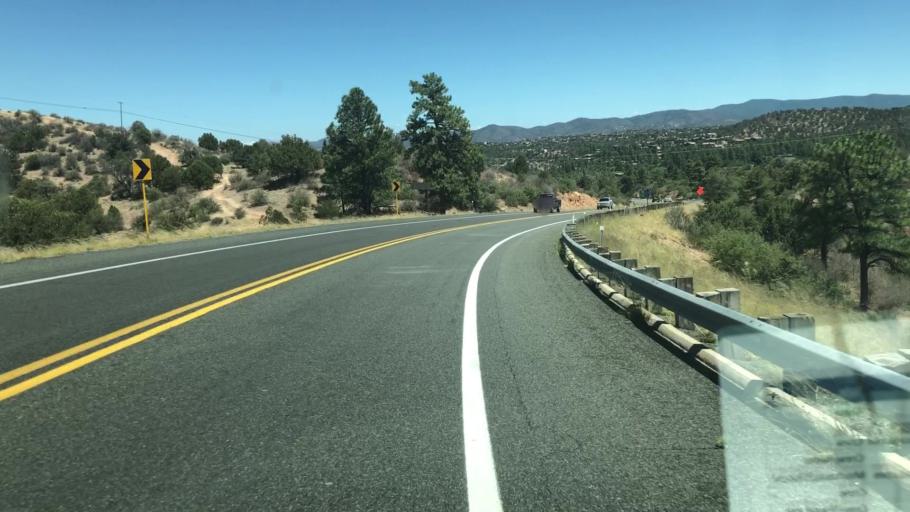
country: US
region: Arizona
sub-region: Yavapai County
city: Prescott
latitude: 34.5809
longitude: -112.5323
